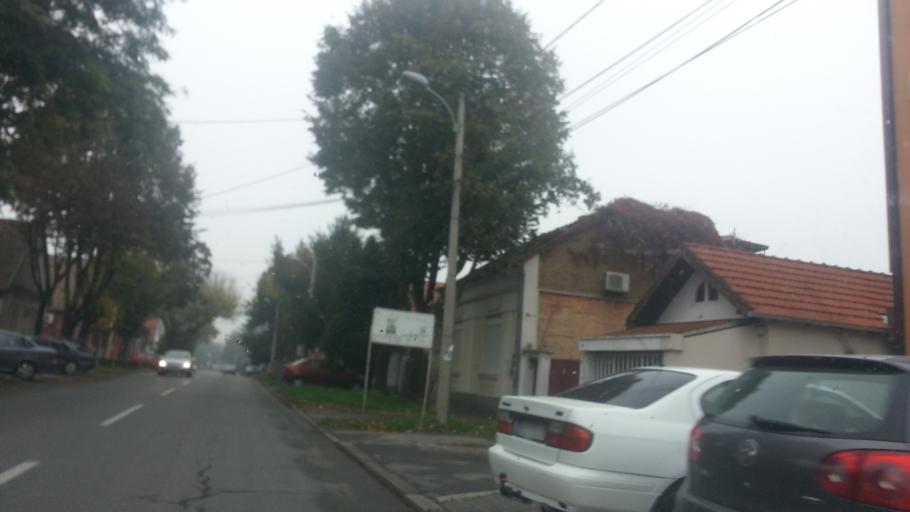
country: RS
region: Central Serbia
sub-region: Belgrade
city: Zemun
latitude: 44.8482
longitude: 20.3863
